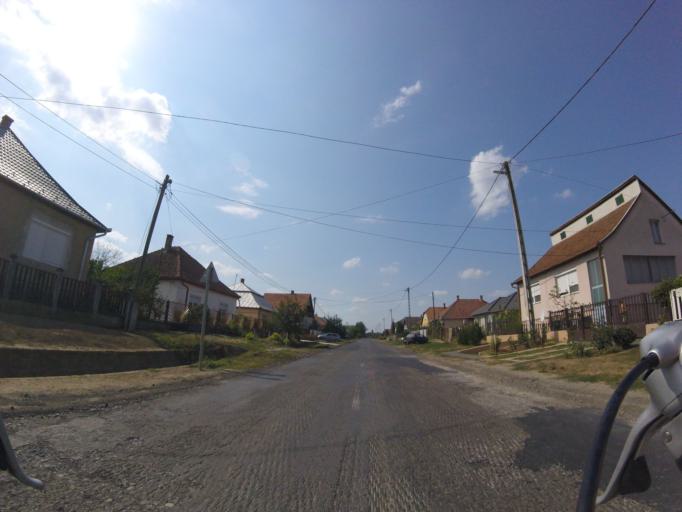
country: HU
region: Szabolcs-Szatmar-Bereg
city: Anarcs
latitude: 48.1618
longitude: 22.1315
